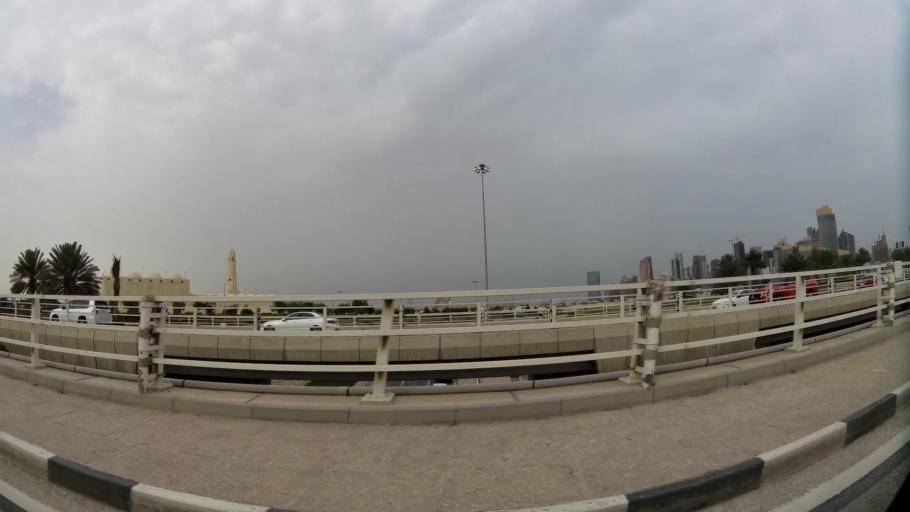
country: QA
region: Baladiyat ad Dawhah
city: Doha
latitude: 25.3136
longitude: 51.5059
